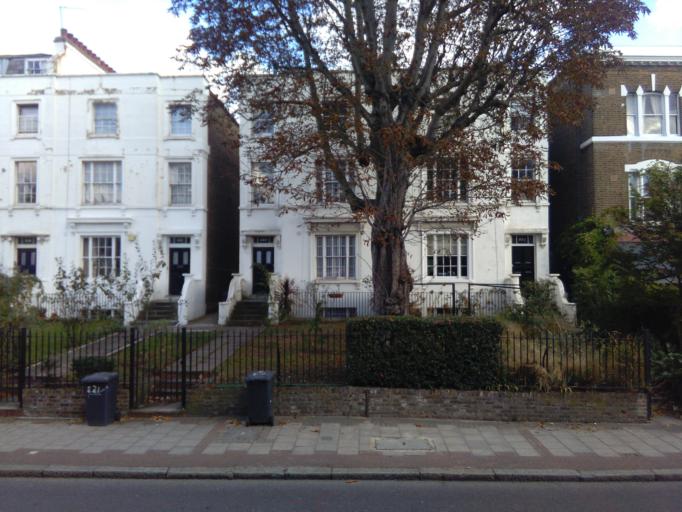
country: GB
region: England
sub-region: Greater London
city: Brixton
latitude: 51.4726
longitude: -0.1126
